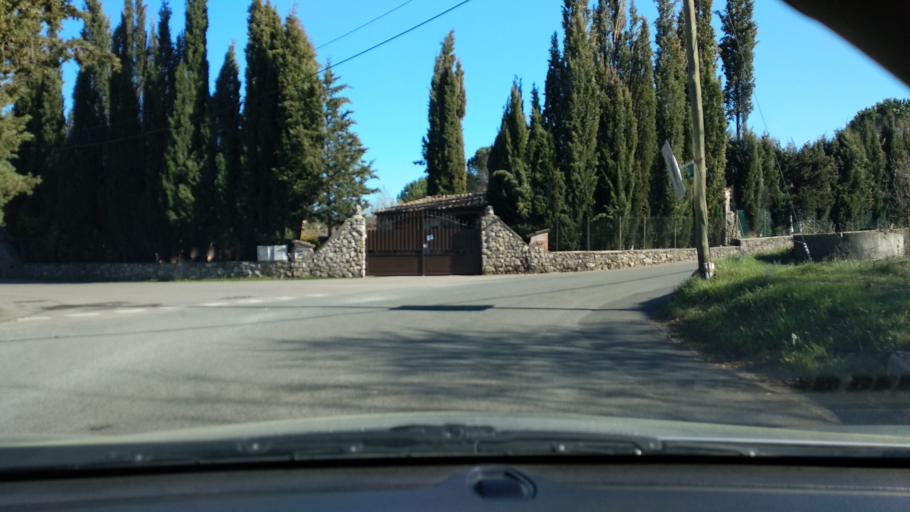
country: FR
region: Provence-Alpes-Cote d'Azur
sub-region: Departement des Alpes-Maritimes
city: Saint-Cezaire-sur-Siagne
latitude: 43.6511
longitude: 6.8003
